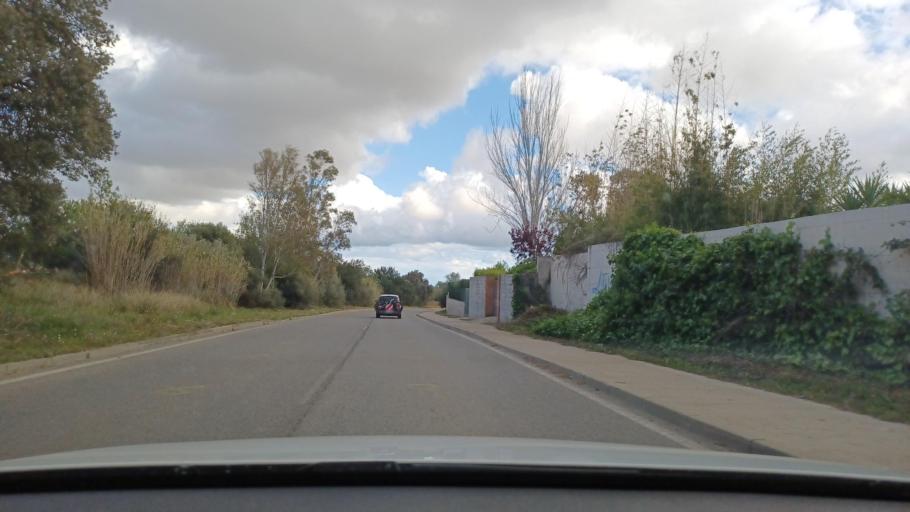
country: ES
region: Catalonia
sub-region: Provincia de Tarragona
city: Botarell
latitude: 41.1348
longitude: 0.9925
